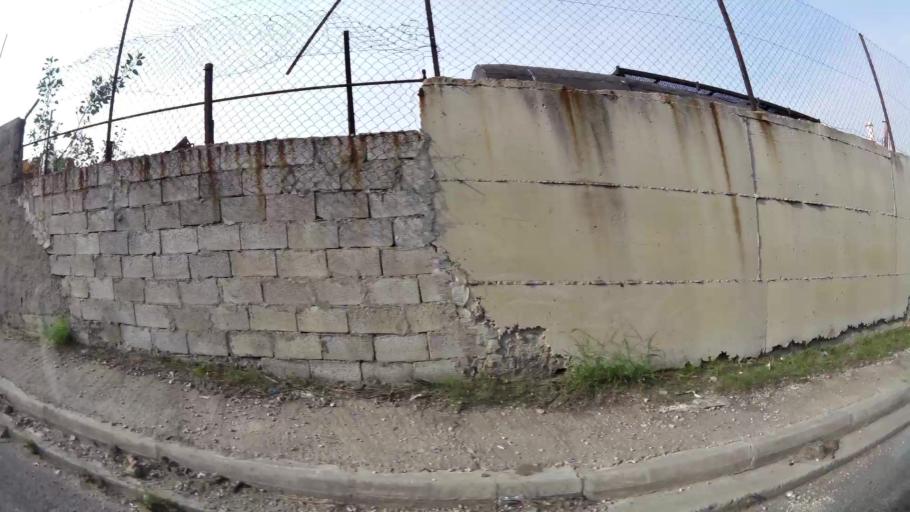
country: GR
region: Attica
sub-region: Nomarchia Athinas
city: Skaramangas
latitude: 38.0286
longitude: 23.6112
